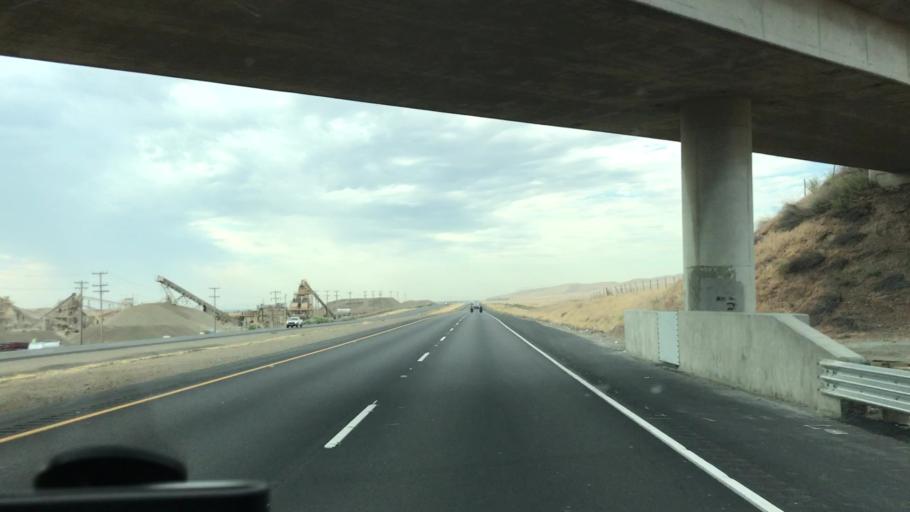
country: US
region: California
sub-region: San Joaquin County
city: Tracy
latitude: 37.6119
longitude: -121.3611
